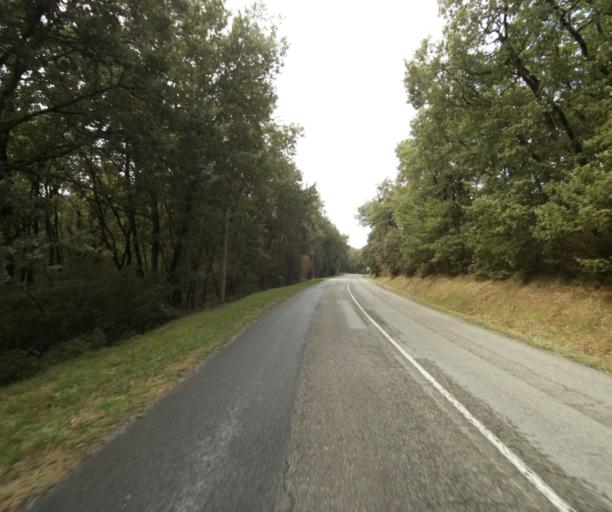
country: FR
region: Midi-Pyrenees
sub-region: Departement du Tarn-et-Garonne
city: Beaumont-de-Lomagne
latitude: 43.8649
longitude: 1.0929
